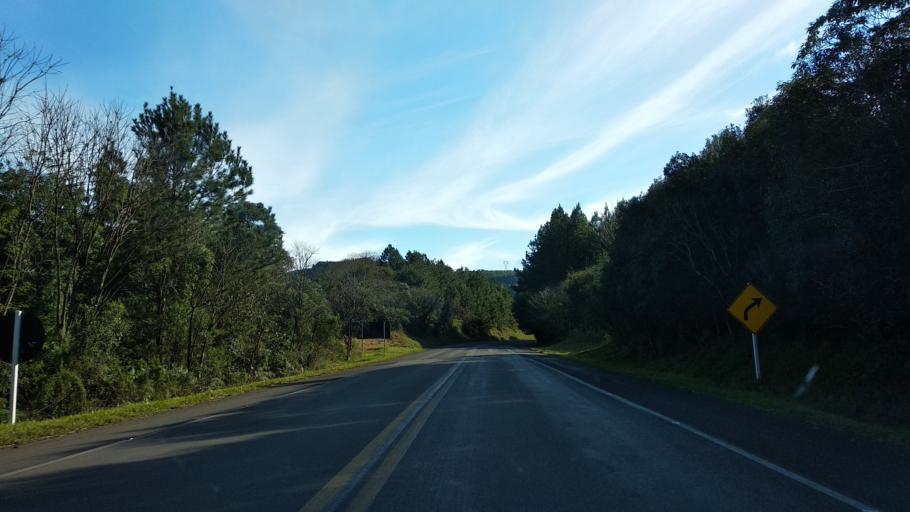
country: BR
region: Santa Catarina
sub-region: Celso Ramos
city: Celso Ramos
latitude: -27.5497
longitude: -51.4434
